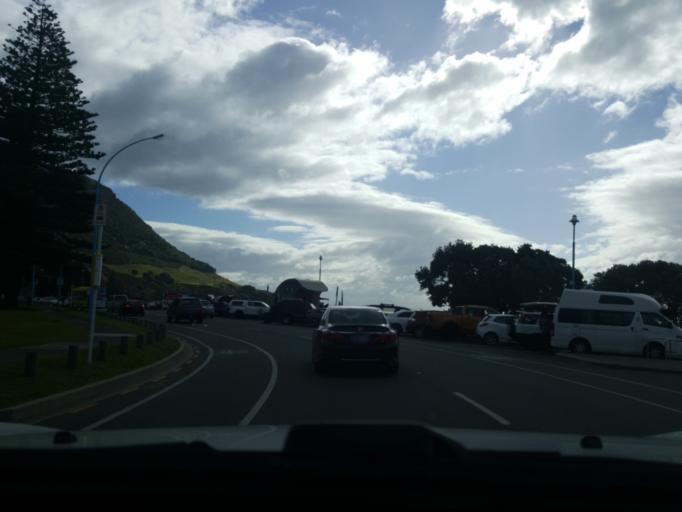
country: NZ
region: Bay of Plenty
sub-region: Tauranga City
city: Tauranga
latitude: -37.6337
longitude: 176.1841
